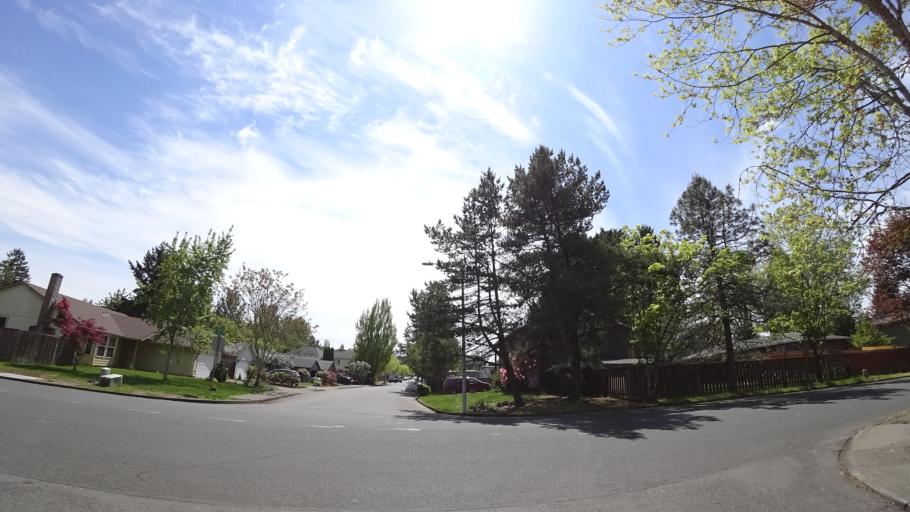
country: US
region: Oregon
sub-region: Washington County
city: Aloha
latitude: 45.4773
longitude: -122.8907
